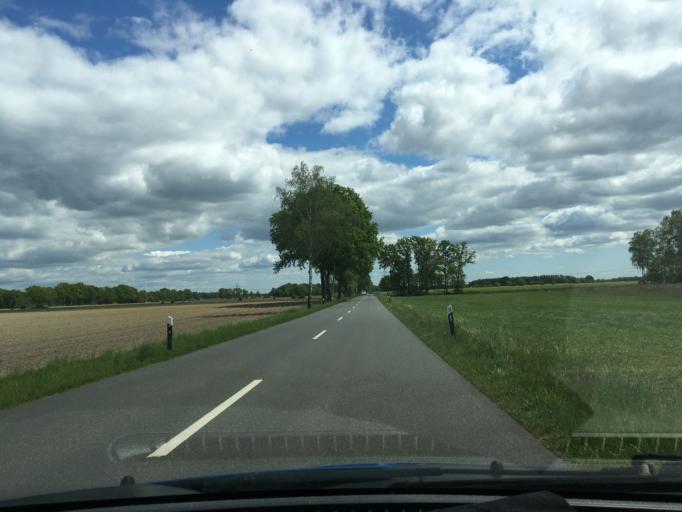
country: DE
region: Lower Saxony
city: Suderburg
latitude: 52.9297
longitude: 10.4555
